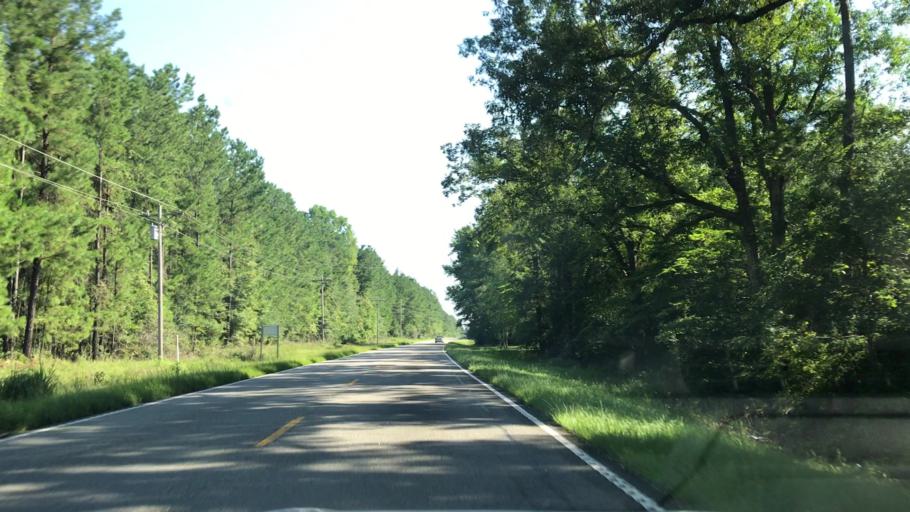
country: US
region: South Carolina
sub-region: Georgetown County
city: Georgetown
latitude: 33.4950
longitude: -79.2623
